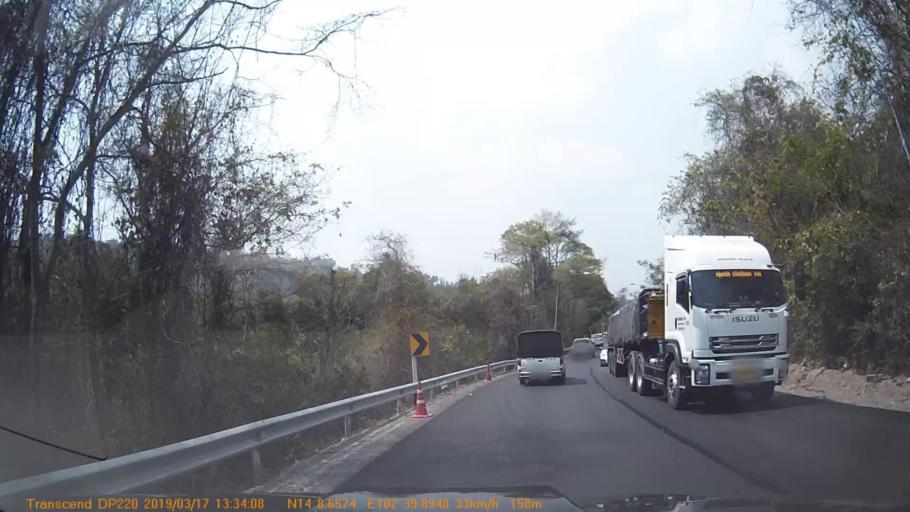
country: TH
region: Buriram
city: Non Din Daeng
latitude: 14.1444
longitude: 102.6647
